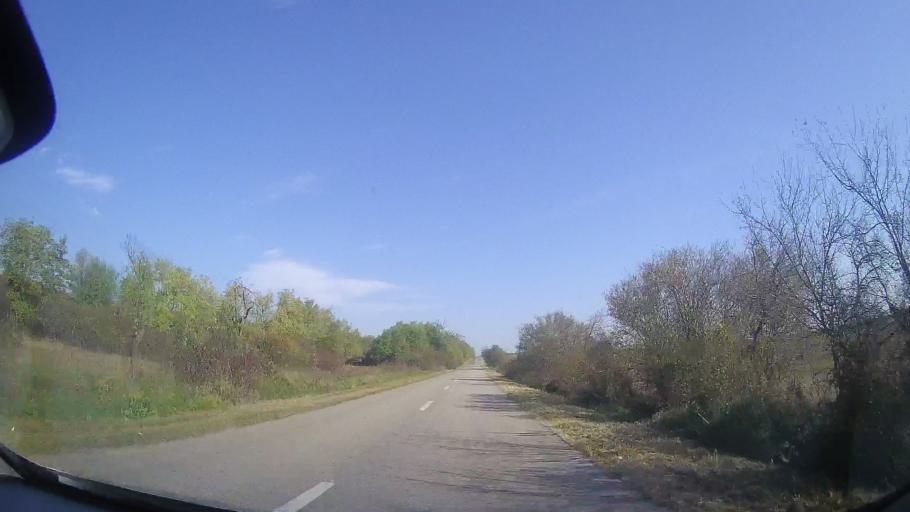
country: RO
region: Timis
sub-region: Comuna Ghizela
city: Ghizela
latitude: 45.8118
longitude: 21.7222
